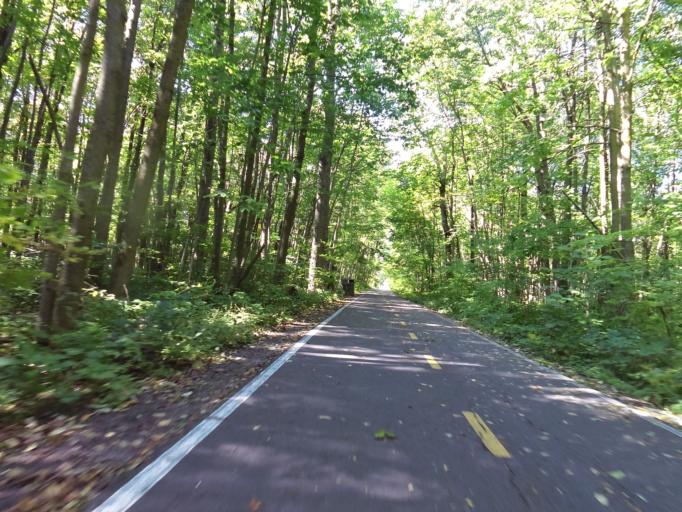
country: CA
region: Ontario
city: Bourget
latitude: 45.2664
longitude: -75.3376
